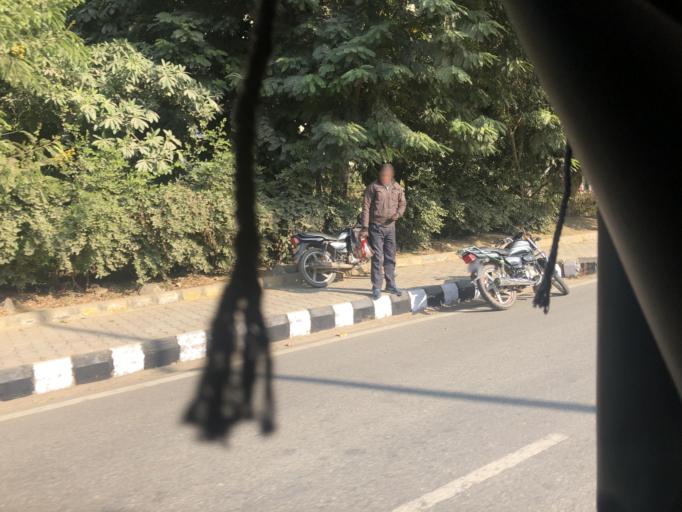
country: IN
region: Haryana
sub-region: Gurgaon
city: Gurgaon
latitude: 28.4492
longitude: 77.0780
